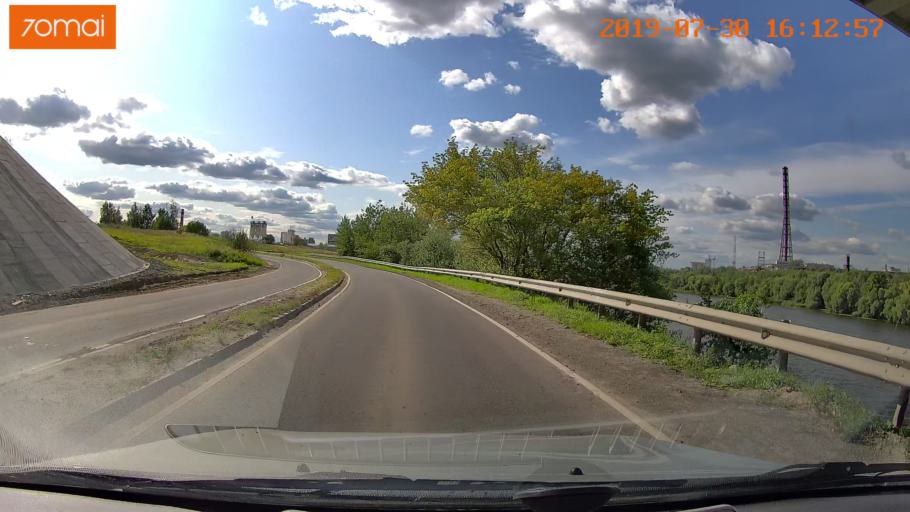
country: RU
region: Moskovskaya
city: Voskresensk
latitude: 55.2906
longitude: 38.6950
